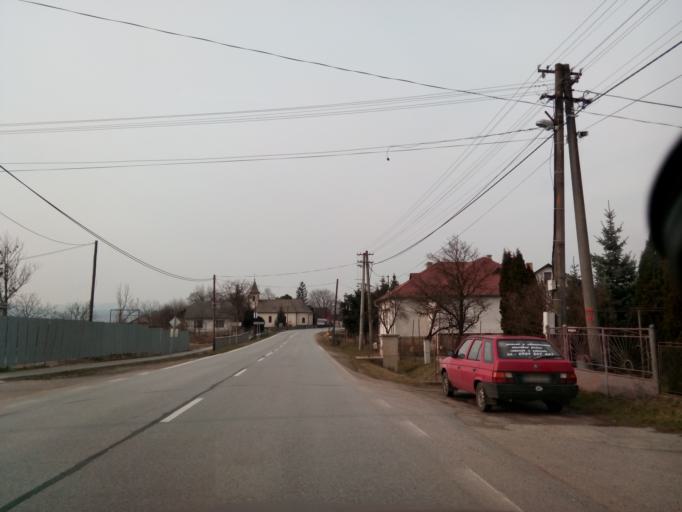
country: HU
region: Borsod-Abauj-Zemplen
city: Satoraljaujhely
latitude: 48.4621
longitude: 21.6411
